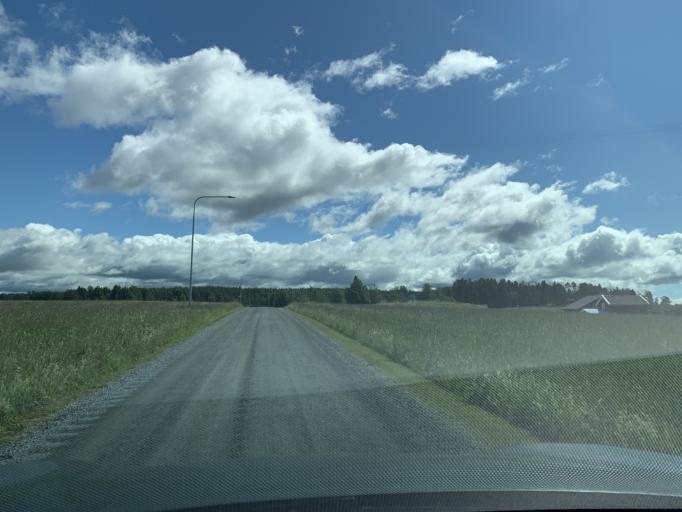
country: SE
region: Jaemtland
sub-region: Krokoms Kommun
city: Krokom
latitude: 63.1477
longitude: 14.3444
